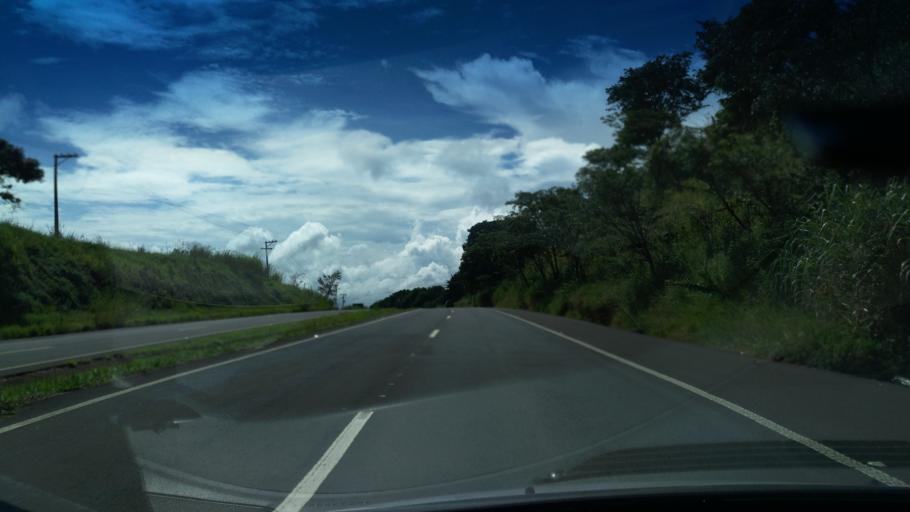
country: BR
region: Sao Paulo
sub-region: Santo Antonio Do Jardim
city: Espirito Santo do Pinhal
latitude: -22.1793
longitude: -46.7537
